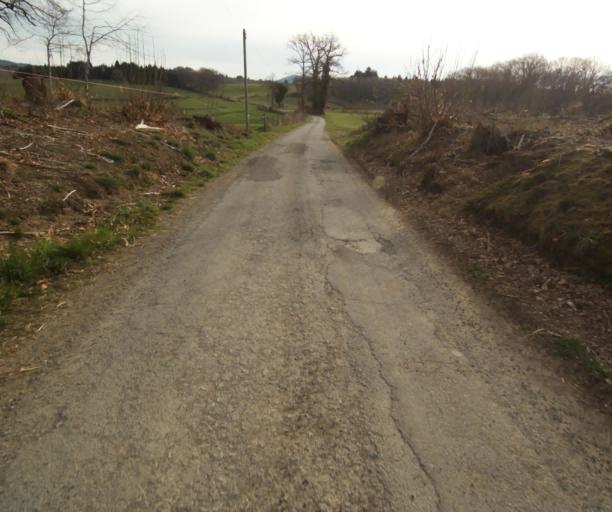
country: FR
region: Limousin
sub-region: Departement de la Correze
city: Chamboulive
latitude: 45.4616
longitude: 1.7612
